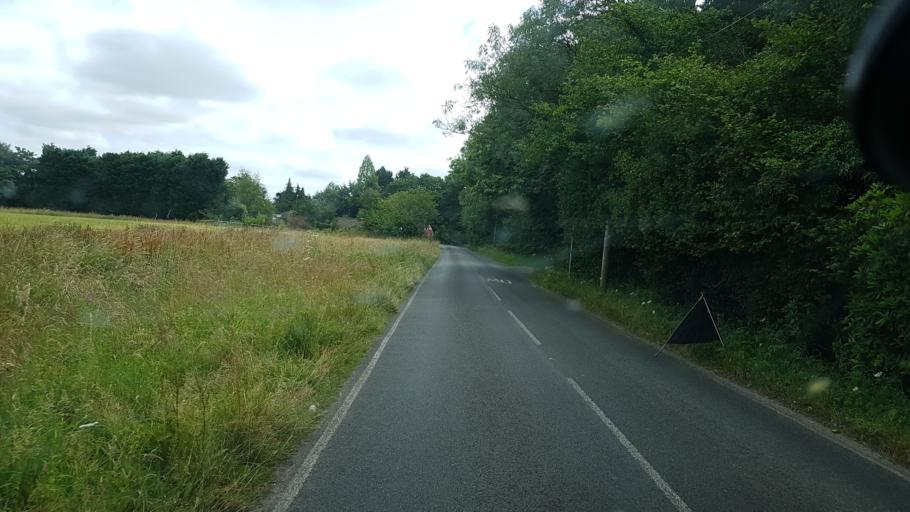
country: GB
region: England
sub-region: Surrey
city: Felbridge
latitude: 51.1179
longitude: -0.0355
